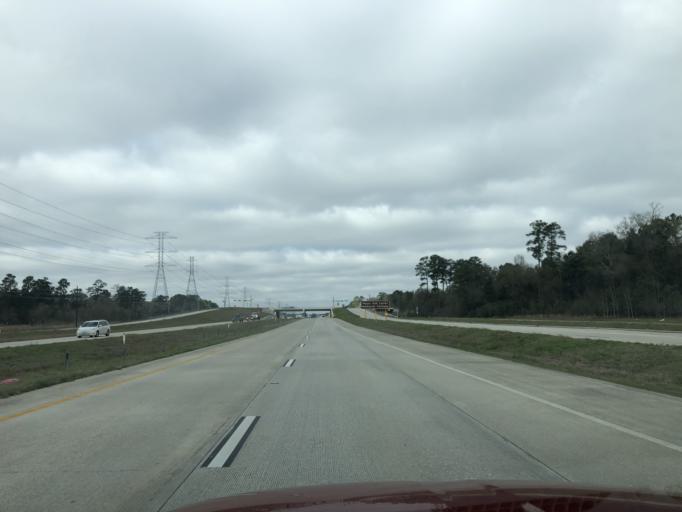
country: US
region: Texas
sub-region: Harris County
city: Spring
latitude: 30.0885
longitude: -95.4533
